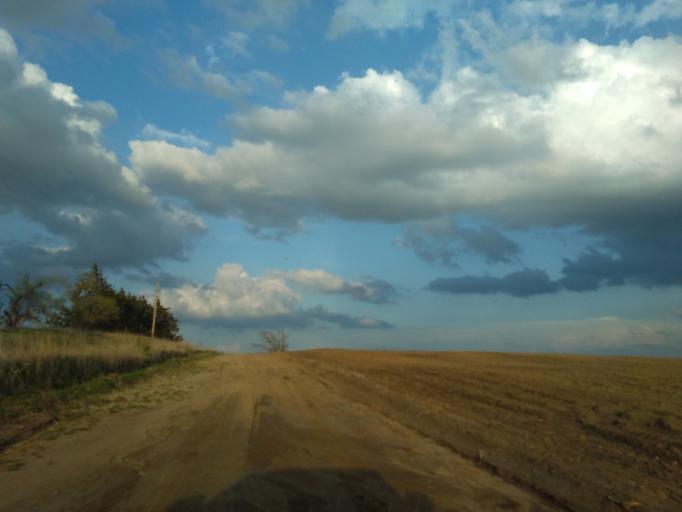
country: US
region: Nebraska
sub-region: Webster County
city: Red Cloud
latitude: 40.2054
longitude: -98.3940
